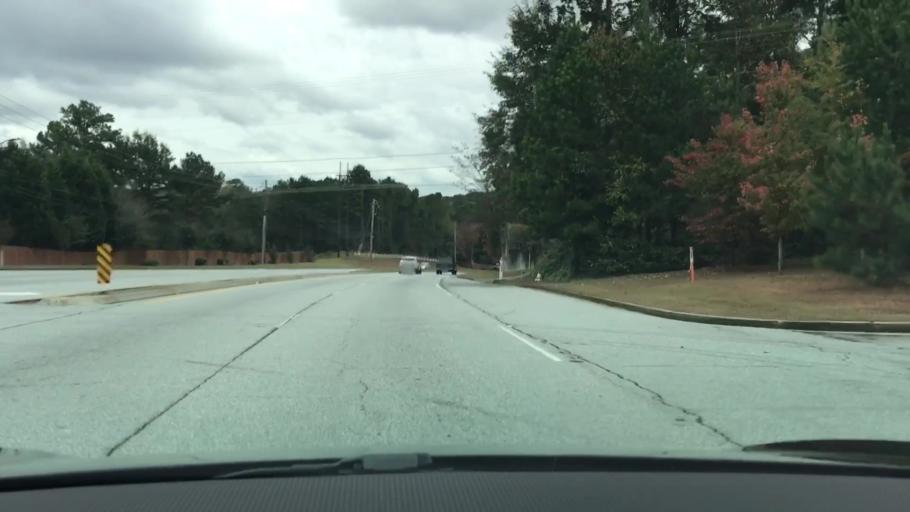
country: US
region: Georgia
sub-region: Gwinnett County
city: Lawrenceville
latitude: 33.9831
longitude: -84.0218
